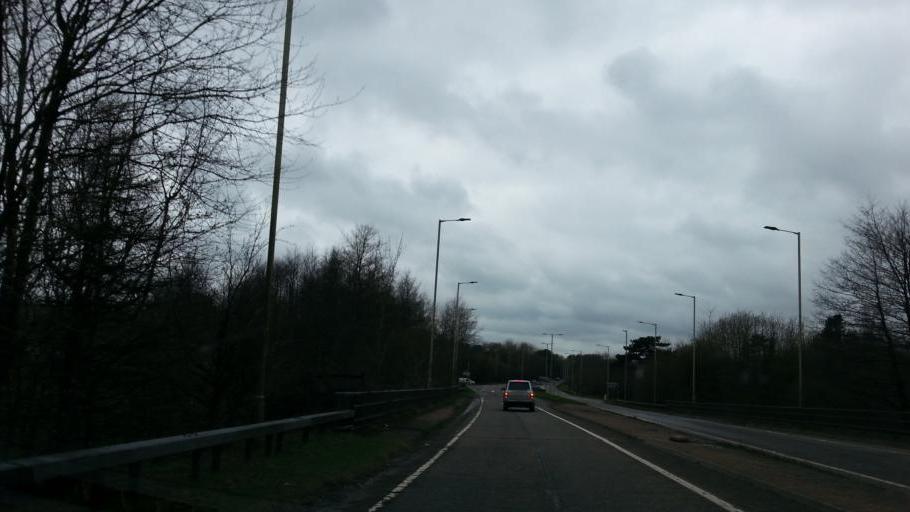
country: GB
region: England
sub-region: Devon
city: South Molton
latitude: 51.0280
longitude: -3.8228
